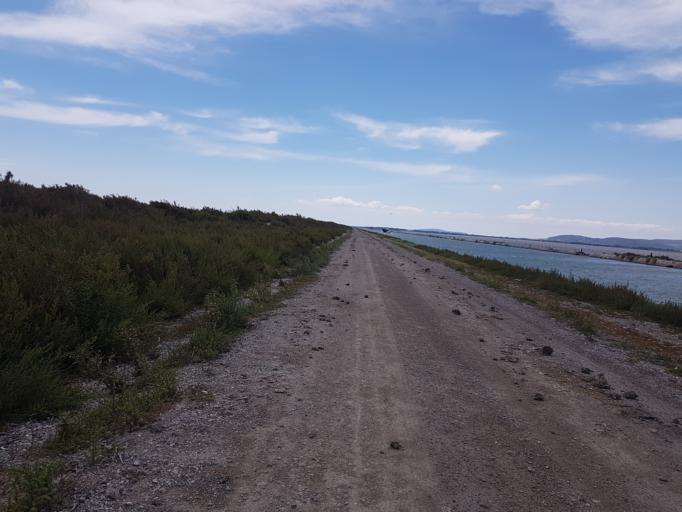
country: FR
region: Languedoc-Roussillon
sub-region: Departement de l'Herault
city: Villeneuve-les-Maguelone
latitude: 43.4990
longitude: 3.8573
